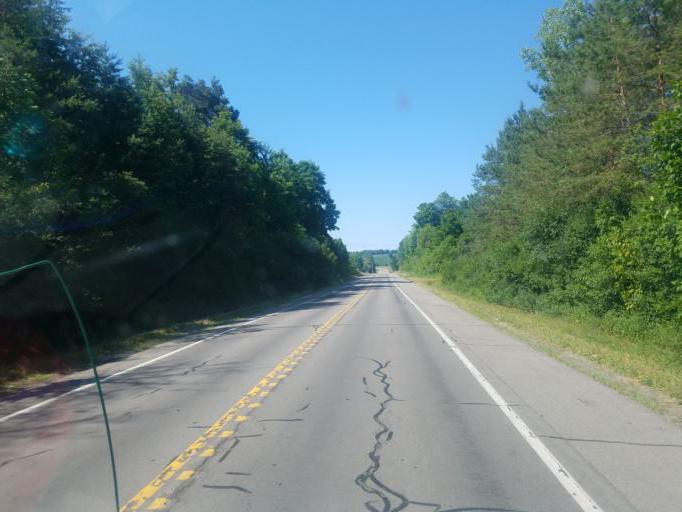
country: US
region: New York
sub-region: Ontario County
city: Phelps
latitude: 42.9710
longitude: -77.0758
